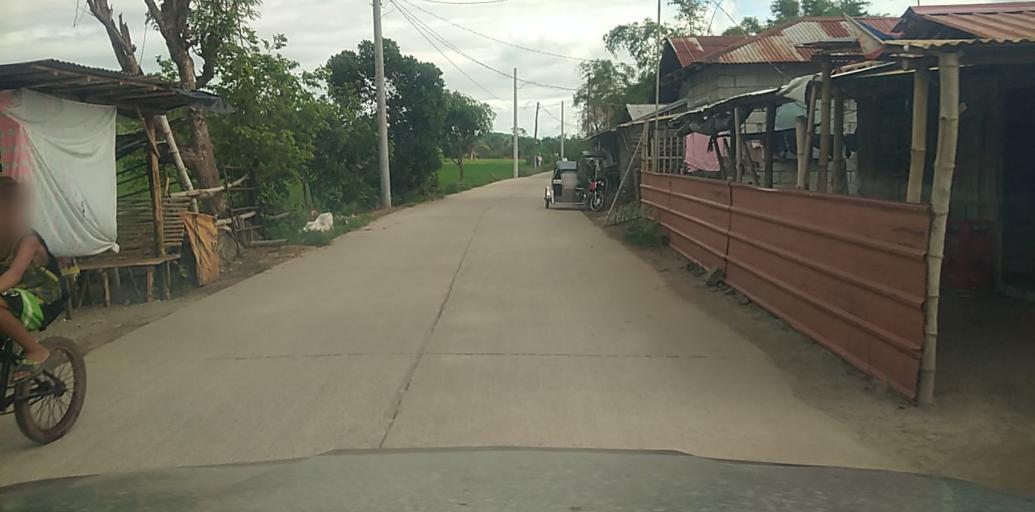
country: PH
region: Central Luzon
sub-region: Province of Pampanga
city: Panlinlang
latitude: 15.1814
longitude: 120.6989
